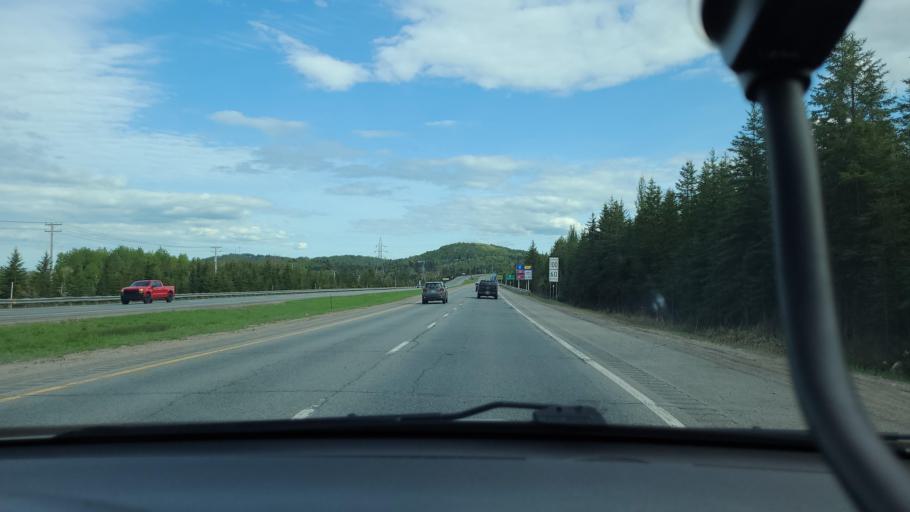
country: CA
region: Quebec
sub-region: Laurentides
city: Sainte-Agathe-des-Monts
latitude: 46.0552
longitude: -74.2721
